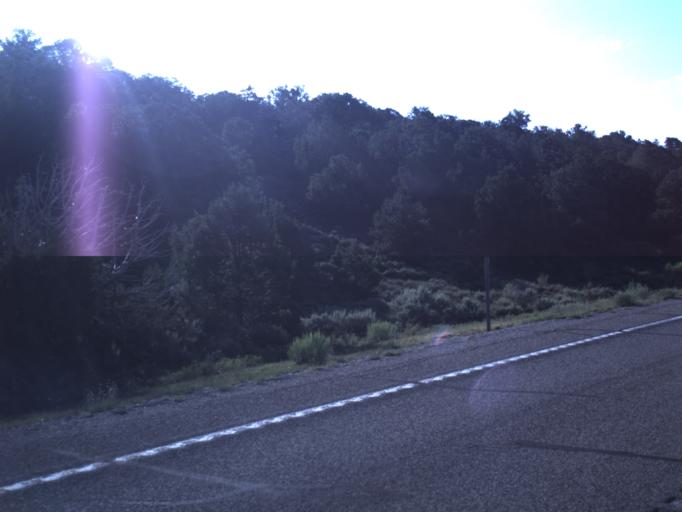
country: US
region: Utah
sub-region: Wayne County
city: Loa
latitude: 38.6984
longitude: -111.3974
